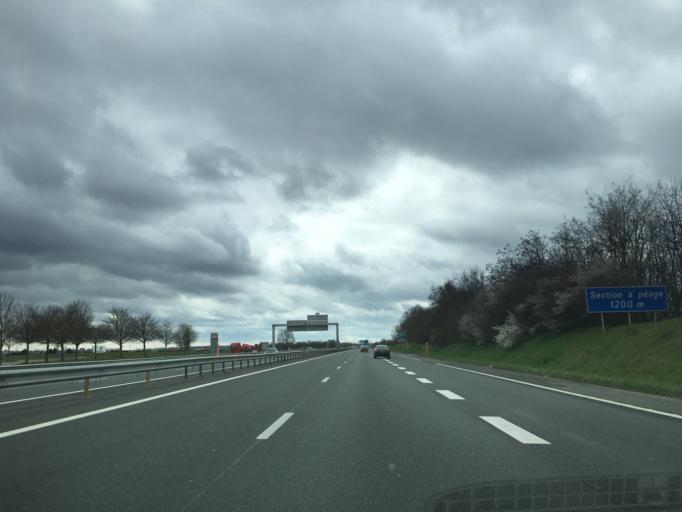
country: FR
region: Ile-de-France
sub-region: Departement de Seine-et-Marne
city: Moissy-Cramayel
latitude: 48.6105
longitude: 2.6325
